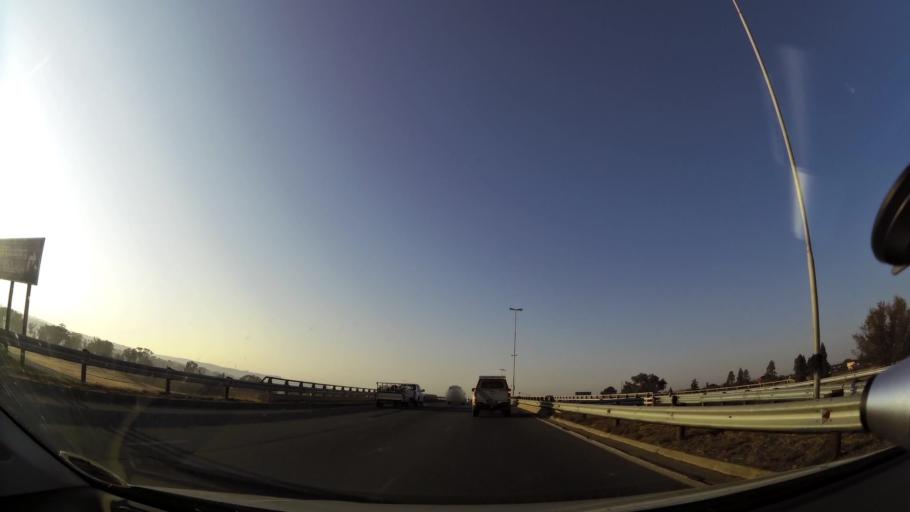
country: ZA
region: Orange Free State
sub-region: Mangaung Metropolitan Municipality
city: Bloemfontein
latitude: -29.0899
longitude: 26.1707
